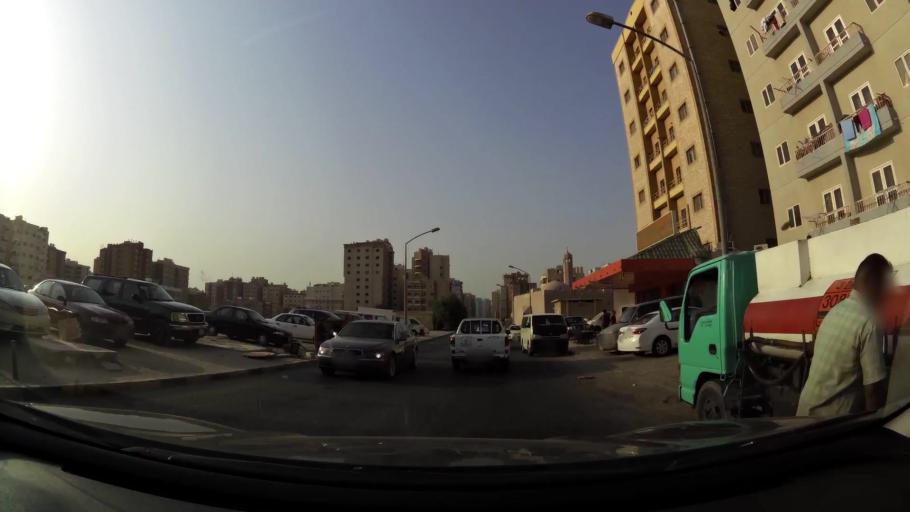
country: KW
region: Muhafazat Hawalli
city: As Salimiyah
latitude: 29.3259
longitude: 48.0641
